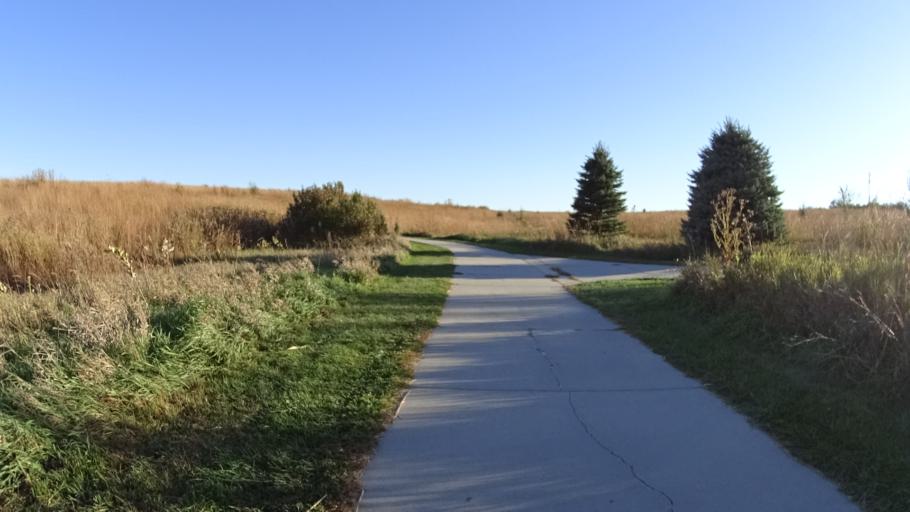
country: US
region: Nebraska
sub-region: Sarpy County
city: Papillion
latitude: 41.1423
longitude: -96.0746
